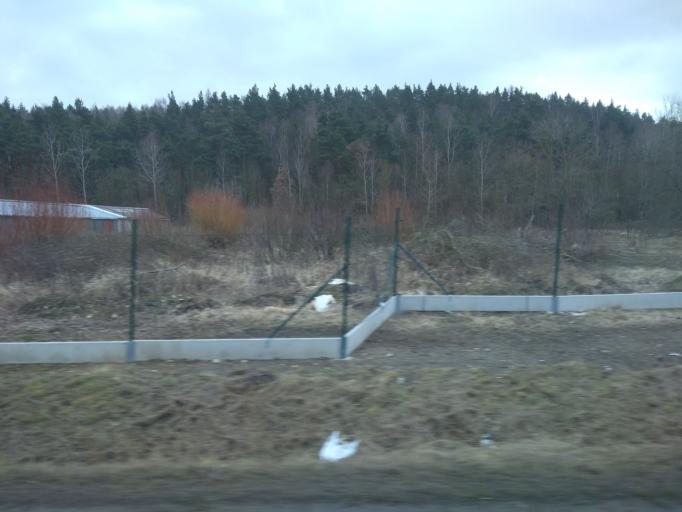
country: CZ
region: Plzensky
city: Vejprnice
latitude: 49.7350
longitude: 13.2966
